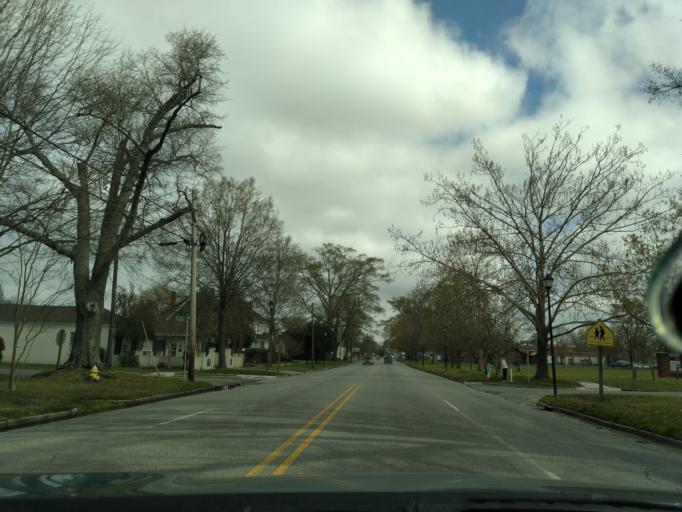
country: US
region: North Carolina
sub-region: Chowan County
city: Edenton
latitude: 36.0658
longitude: -76.6067
